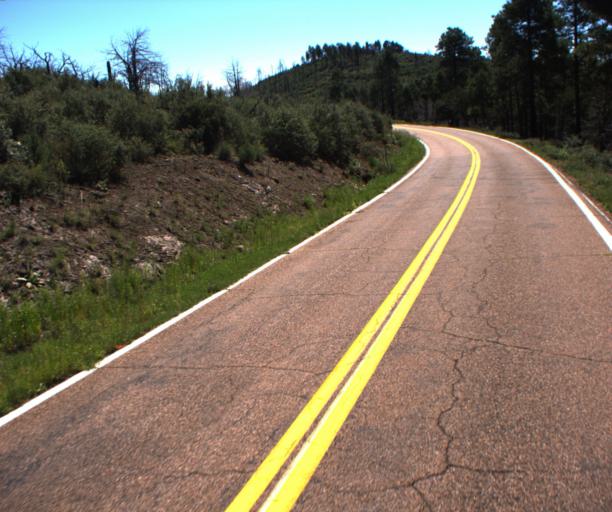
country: US
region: Arizona
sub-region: Greenlee County
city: Morenci
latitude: 33.5302
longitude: -109.3081
